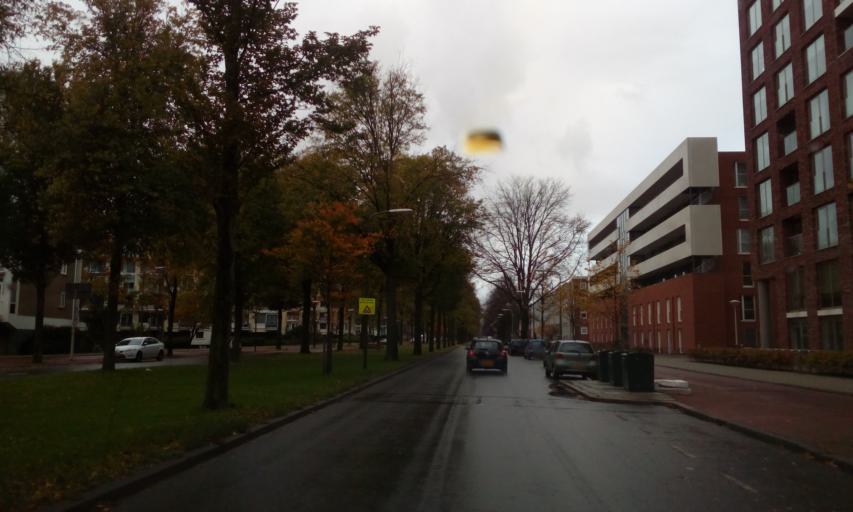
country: NL
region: South Holland
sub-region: Gemeente Westland
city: Kwintsheul
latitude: 52.0506
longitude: 4.2637
